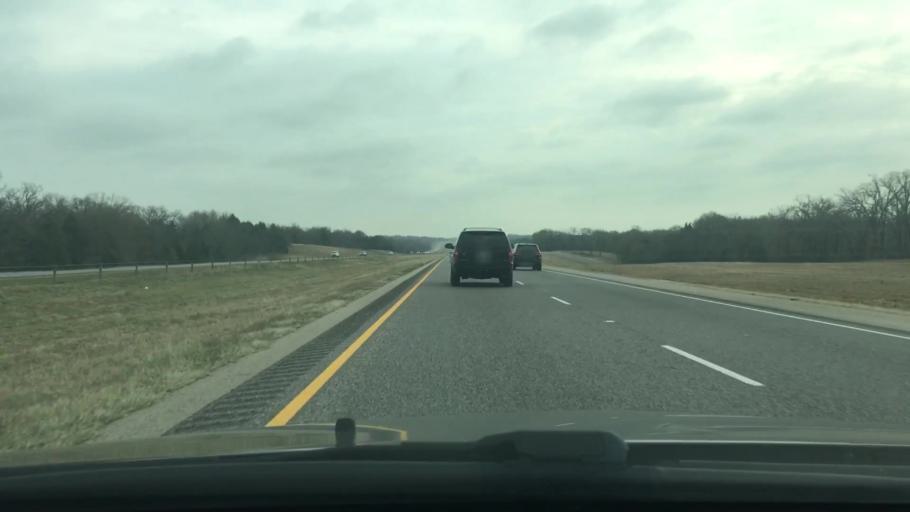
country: US
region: Texas
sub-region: Freestone County
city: Fairfield
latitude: 31.6646
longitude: -96.1625
